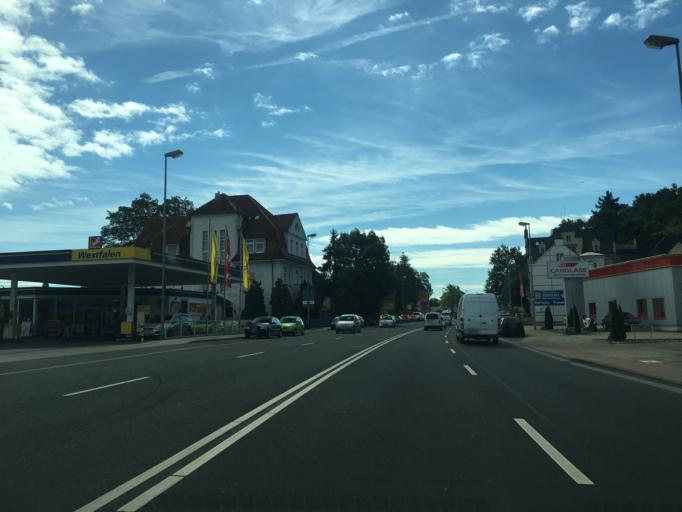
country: DE
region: Lower Saxony
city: Hameln
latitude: 52.0986
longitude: 9.3509
